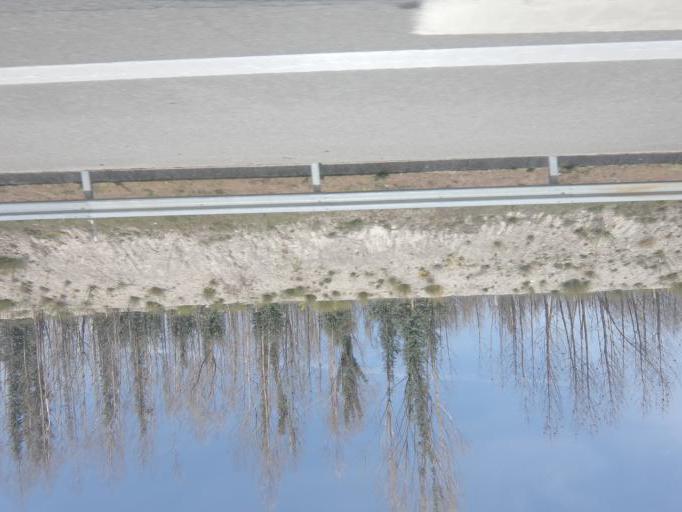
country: PT
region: Viseu
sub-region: Oliveira de Frades
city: Oliveira de Frades
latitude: 40.6848
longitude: -8.2056
